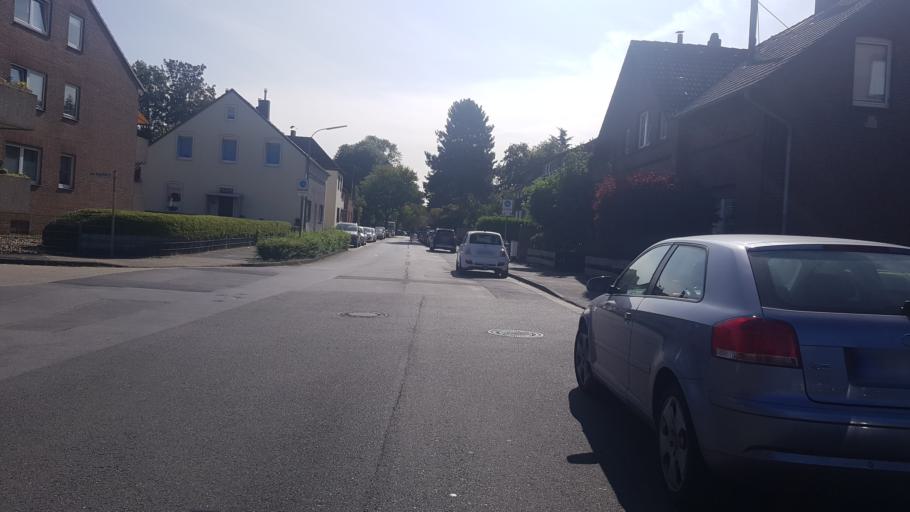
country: DE
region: North Rhine-Westphalia
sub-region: Regierungsbezirk Dusseldorf
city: Ratingen
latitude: 51.3442
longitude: 6.8254
